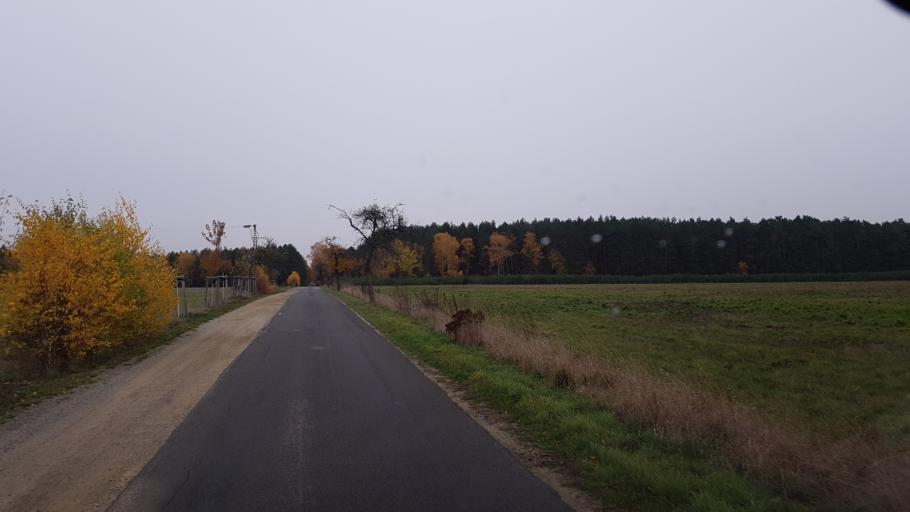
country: DE
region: Brandenburg
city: Crinitz
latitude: 51.7206
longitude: 13.7755
